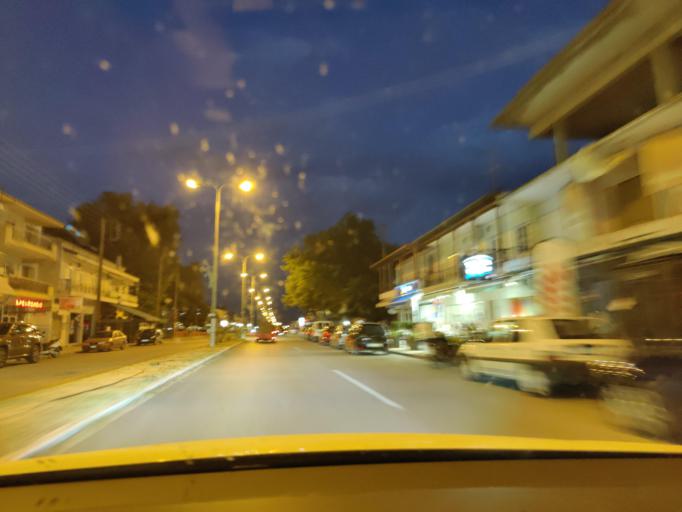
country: GR
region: Central Macedonia
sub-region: Nomos Serron
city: Lefkonas
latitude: 41.0986
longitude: 23.4962
